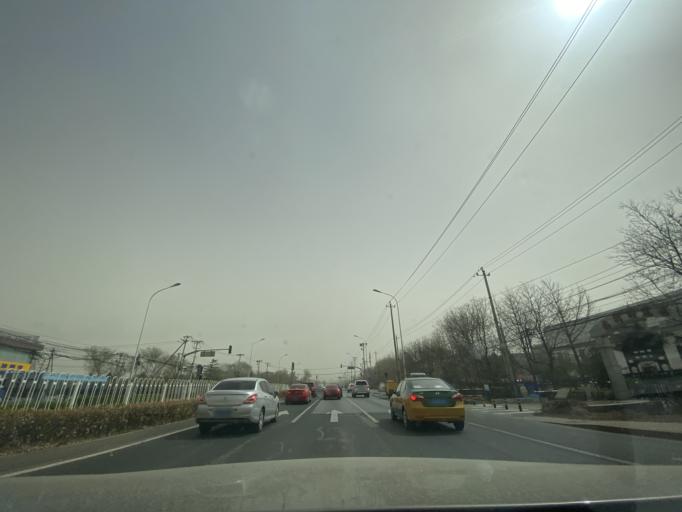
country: CN
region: Beijing
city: Sijiqing
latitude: 39.9460
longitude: 116.2455
